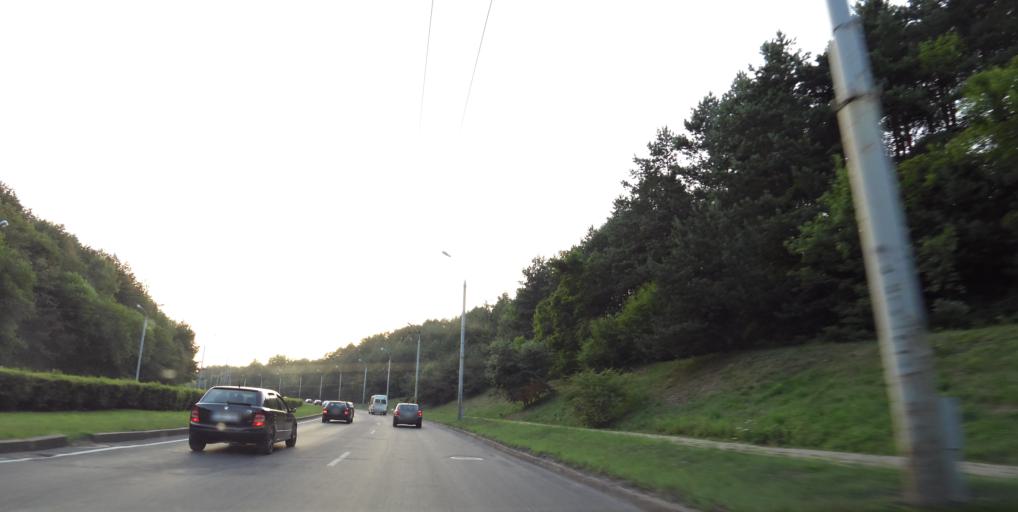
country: LT
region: Vilnius County
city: Seskine
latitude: 54.7002
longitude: 25.2379
